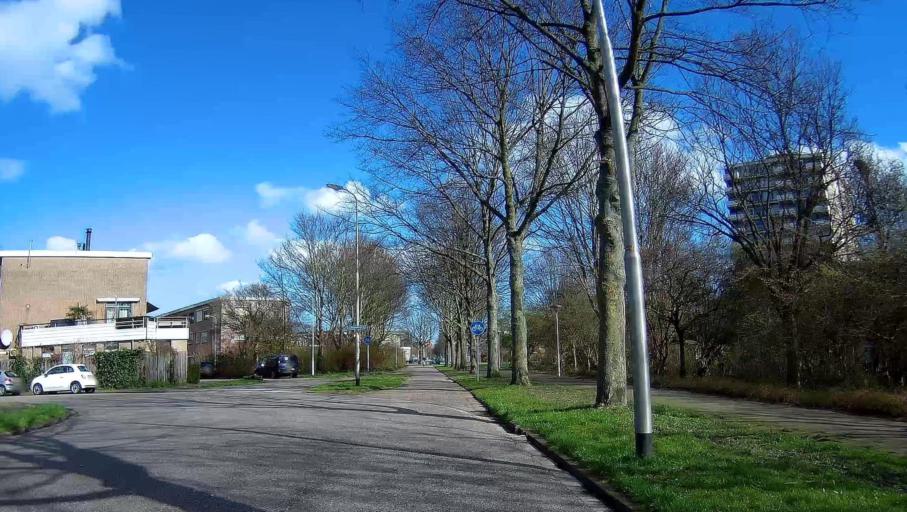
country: NL
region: South Holland
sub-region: Gemeente Zoetermeer
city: Zoetermeer
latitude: 52.0514
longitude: 4.4834
